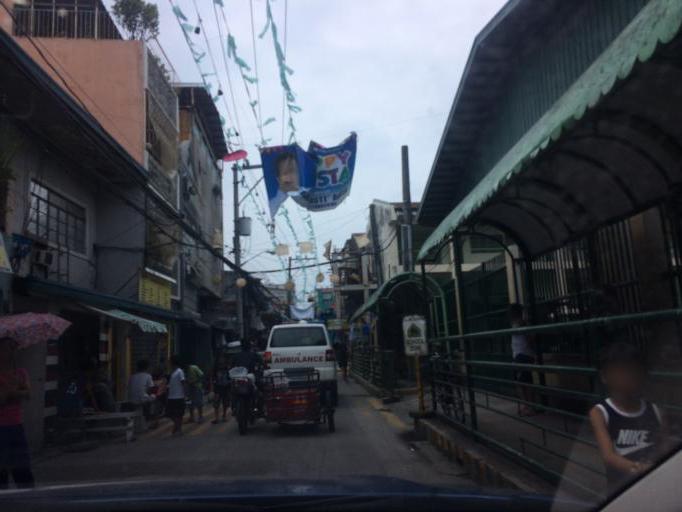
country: PH
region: Metro Manila
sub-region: Makati City
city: Makati City
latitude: 14.5461
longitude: 121.0074
